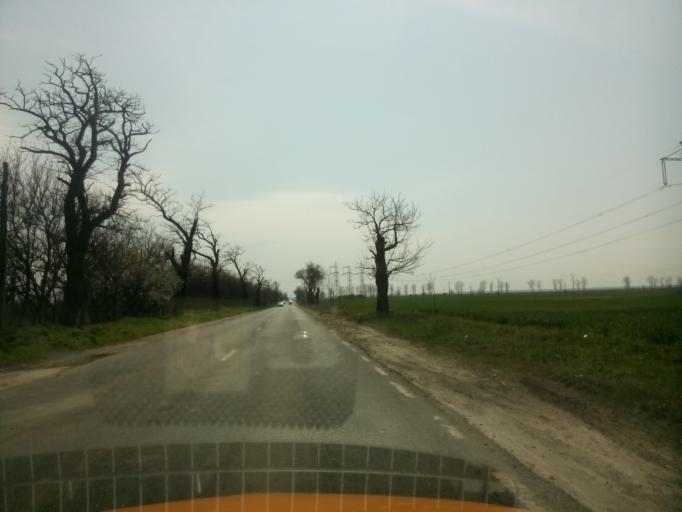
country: RO
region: Giurgiu
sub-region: Comuna Herasti
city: Herasti
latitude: 44.2555
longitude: 26.3635
